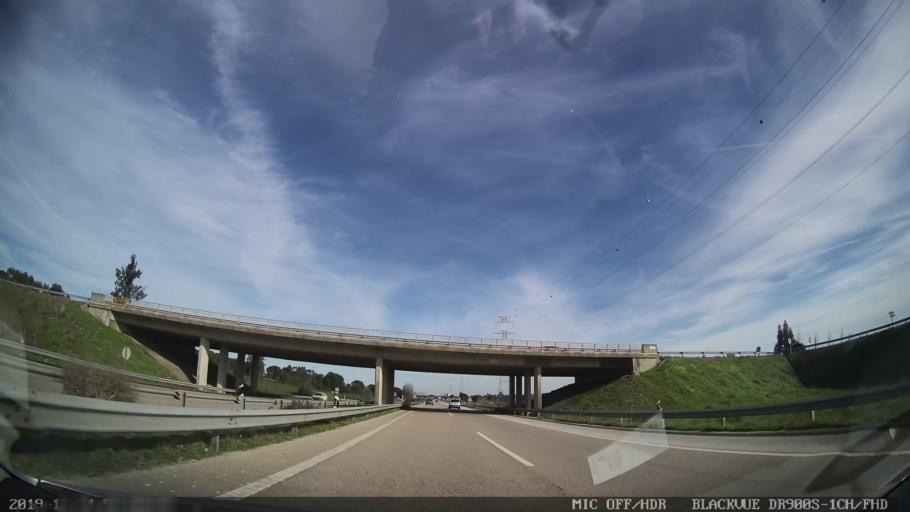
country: PT
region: Santarem
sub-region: Entroncamento
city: Entroncamento
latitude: 39.4743
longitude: -8.4878
